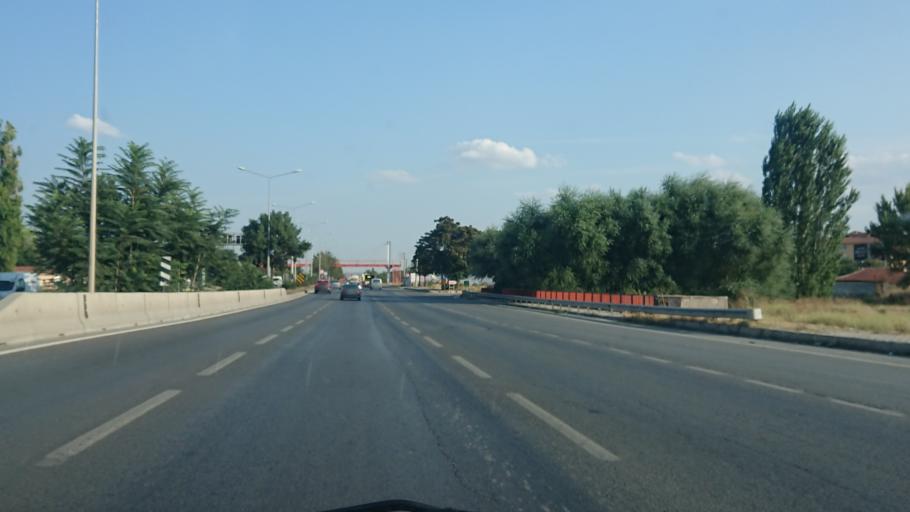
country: TR
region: Eskisehir
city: Eskisehir
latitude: 39.7719
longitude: 30.5591
